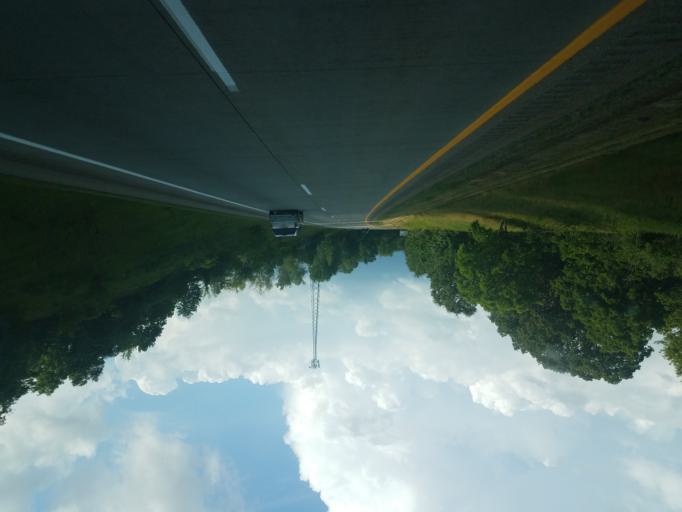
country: US
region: Michigan
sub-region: Calhoun County
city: Marshall
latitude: 42.1611
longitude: -84.9935
